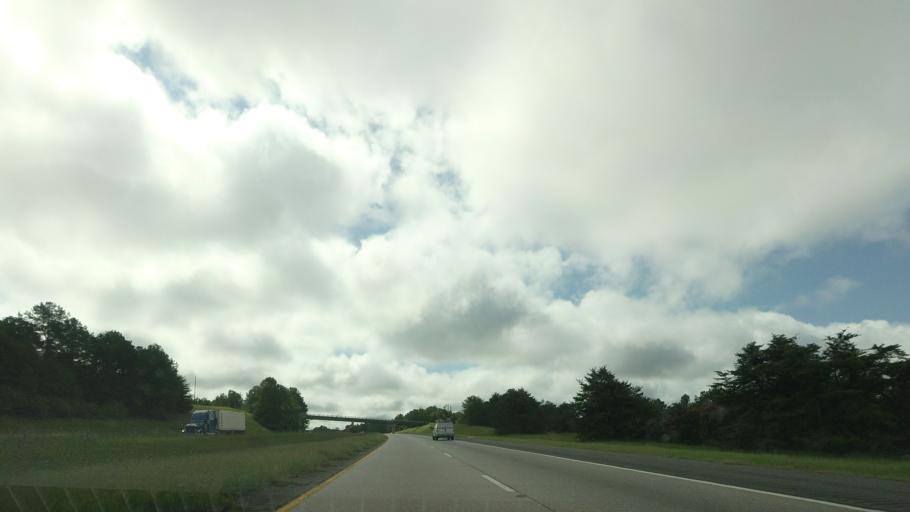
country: US
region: Georgia
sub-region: Houston County
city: Warner Robins
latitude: 32.7223
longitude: -83.5332
